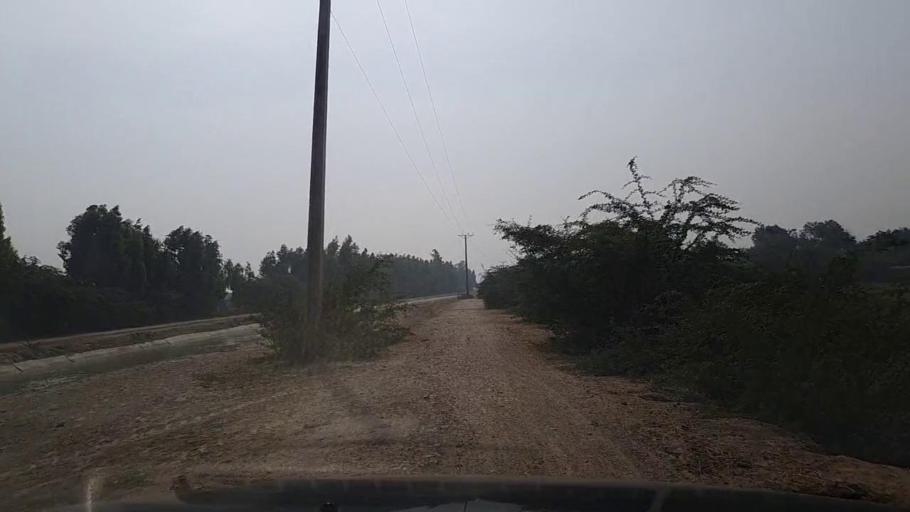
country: PK
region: Sindh
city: Mirpur Sakro
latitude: 24.5376
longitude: 67.8121
